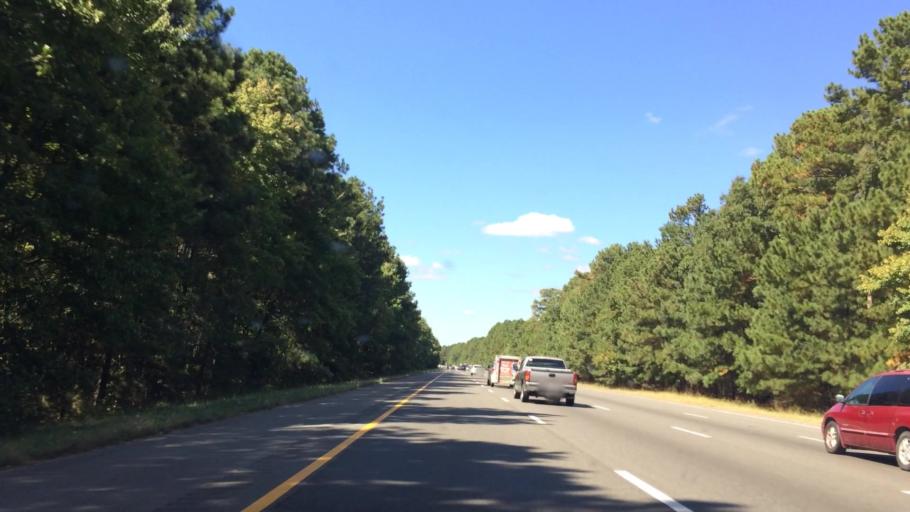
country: US
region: Virginia
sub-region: Henrico County
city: Glen Allen
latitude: 37.6703
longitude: -77.4893
